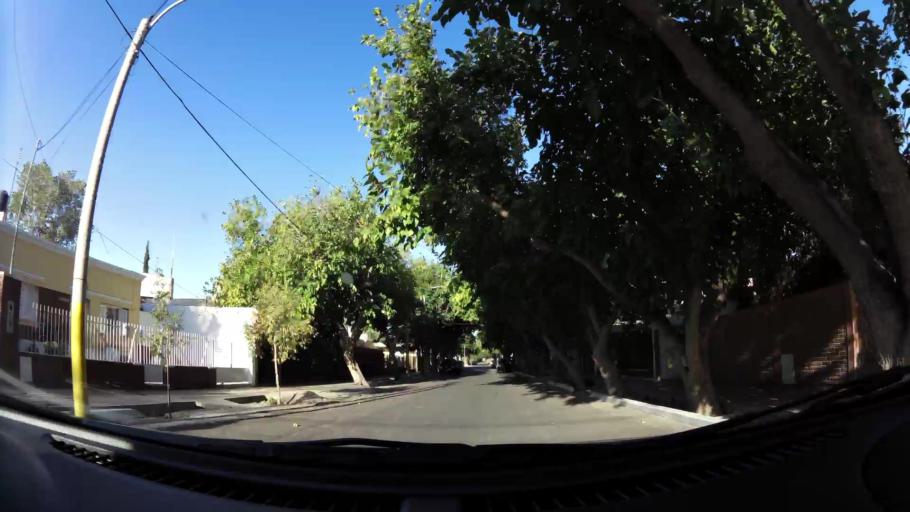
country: AR
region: San Juan
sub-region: Departamento de Santa Lucia
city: Santa Lucia
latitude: -31.5369
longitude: -68.5063
